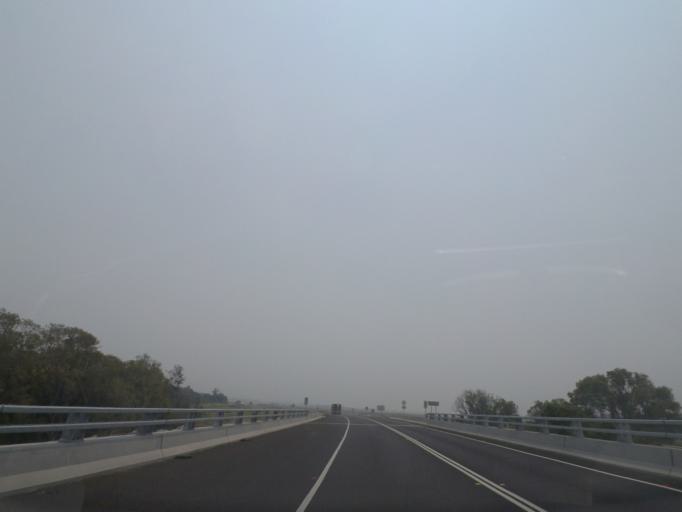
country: AU
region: New South Wales
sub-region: Clarence Valley
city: Maclean
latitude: -29.4052
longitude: 153.2427
